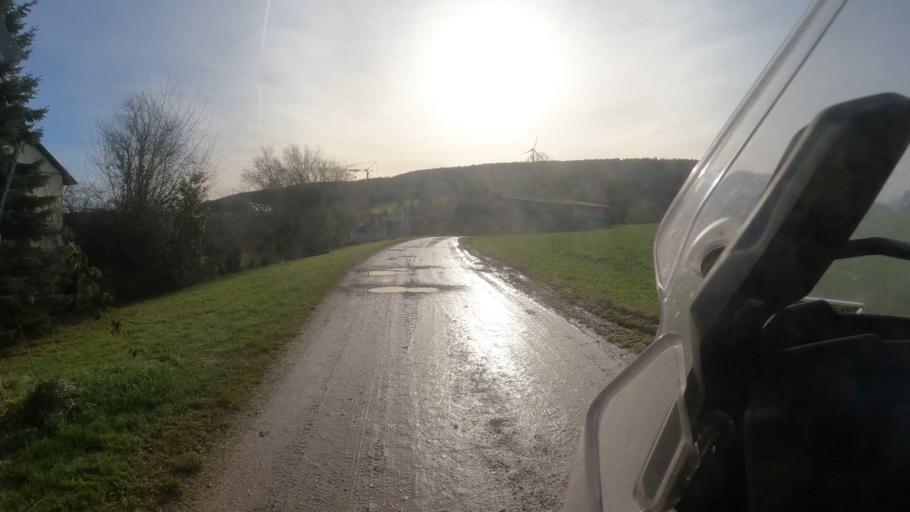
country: DE
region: Baden-Wuerttemberg
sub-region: Freiburg Region
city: Tengen
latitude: 47.7864
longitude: 8.6296
